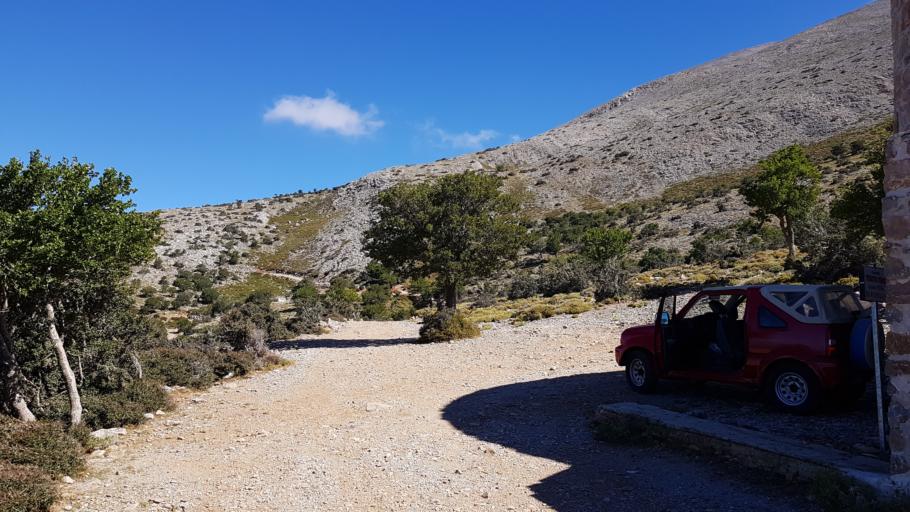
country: GR
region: Crete
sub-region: Nomos Rethymnis
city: Zoniana
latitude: 35.2070
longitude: 24.7618
